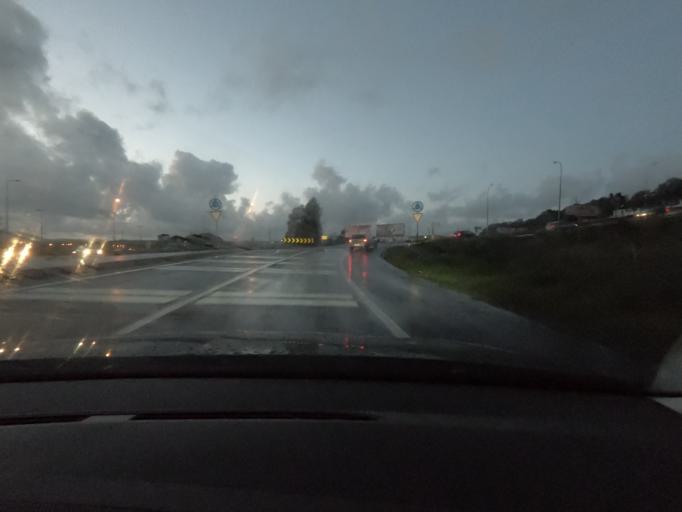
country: PT
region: Lisbon
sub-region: Sintra
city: Cacem
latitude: 38.7465
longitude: -9.3034
